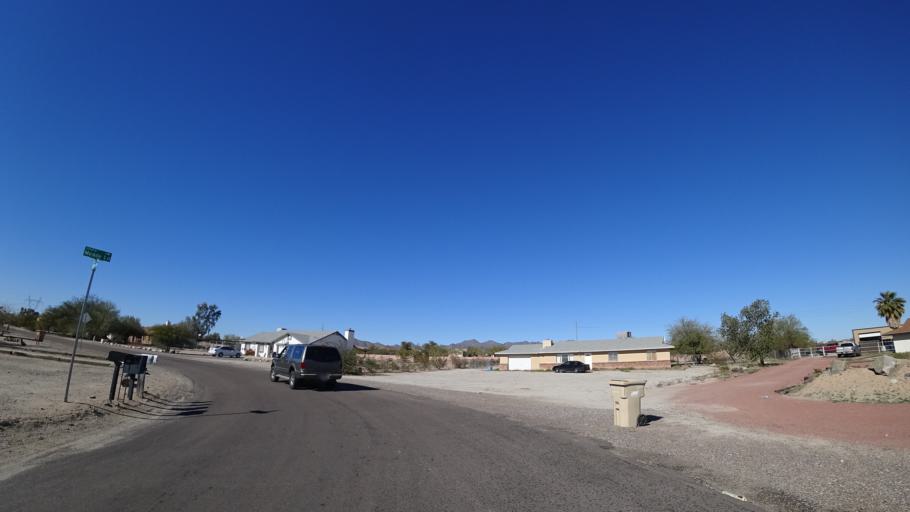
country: US
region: Arizona
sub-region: Maricopa County
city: Buckeye
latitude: 33.4275
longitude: -112.5344
